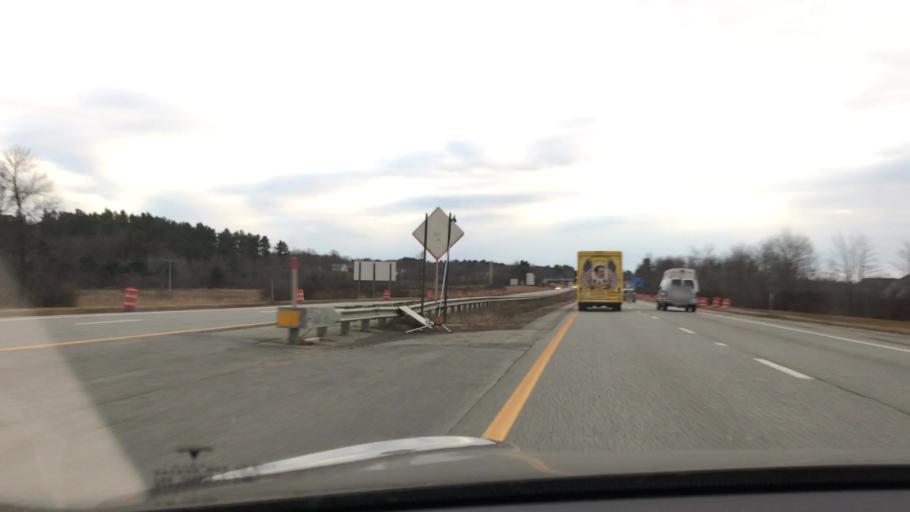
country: US
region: Maine
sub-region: Kennebec County
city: Hallowell
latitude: 44.3038
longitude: -69.8078
